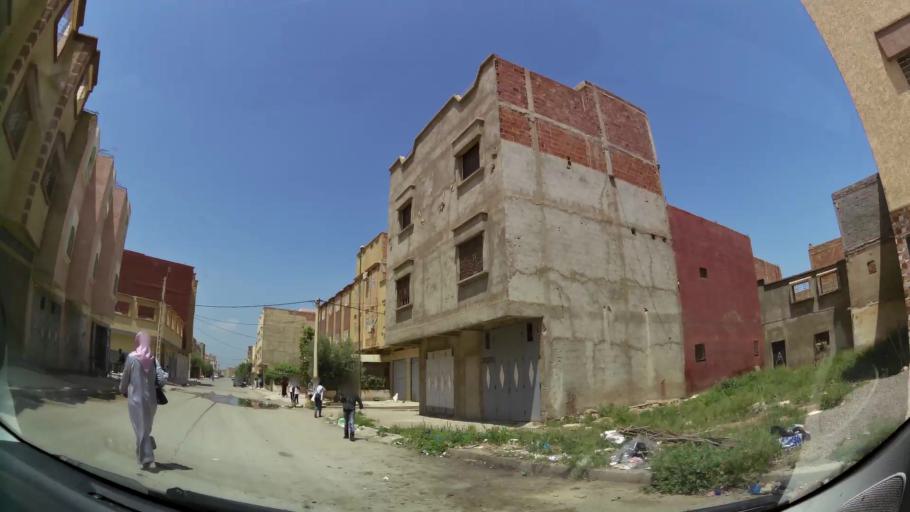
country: MA
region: Oriental
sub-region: Oujda-Angad
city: Oujda
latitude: 34.6862
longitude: -1.8885
